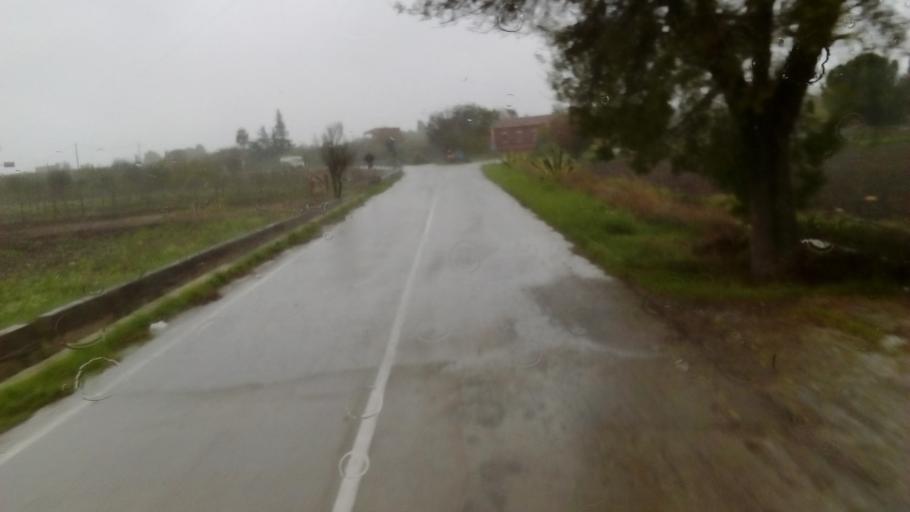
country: IT
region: Sicily
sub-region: Enna
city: Pietraperzia
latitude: 37.4204
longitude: 14.1731
